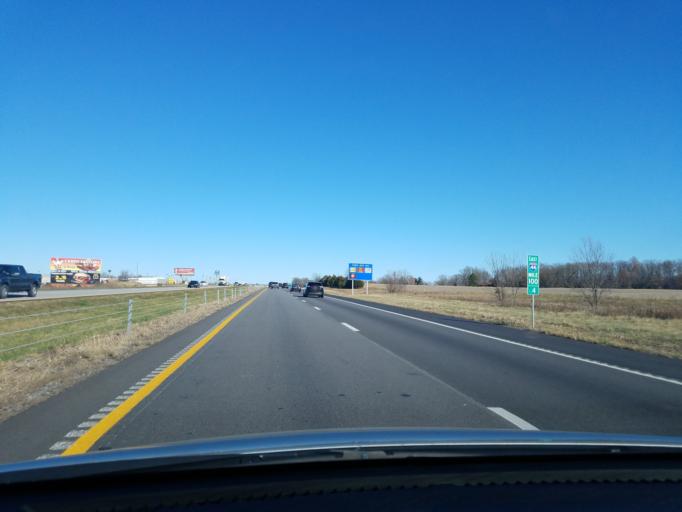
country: US
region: Missouri
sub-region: Webster County
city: Marshfield
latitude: 37.3361
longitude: -92.9380
